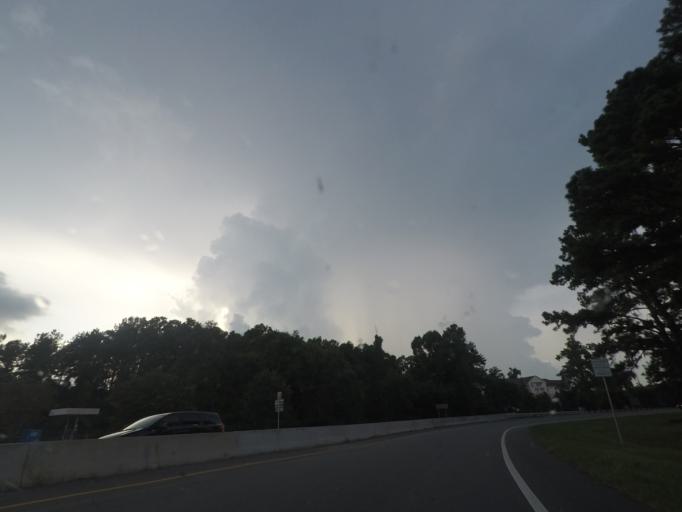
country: US
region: Florida
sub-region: Alachua County
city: Gainesville
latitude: 29.6017
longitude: -82.3745
